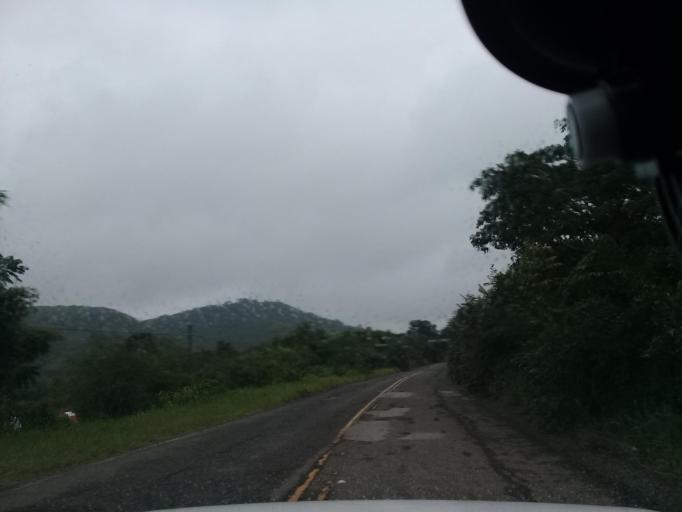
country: MX
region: Veracruz
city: Platon Sanchez
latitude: 21.2246
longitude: -98.3793
